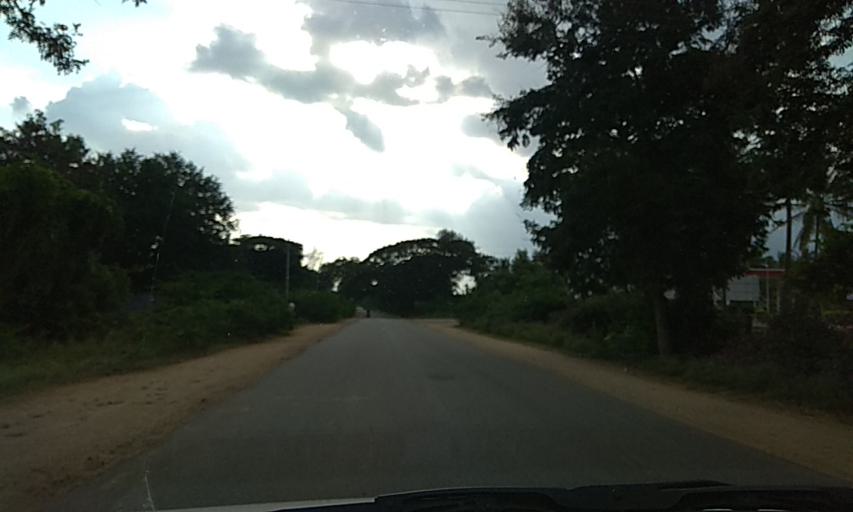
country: IN
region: Karnataka
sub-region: Chamrajnagar
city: Gundlupet
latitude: 11.8110
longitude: 76.7288
